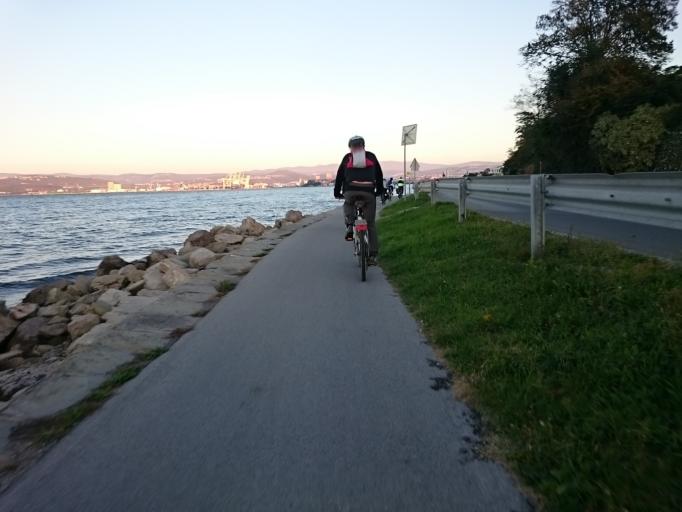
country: SI
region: Koper-Capodistria
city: Koper
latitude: 45.5480
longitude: 13.7008
